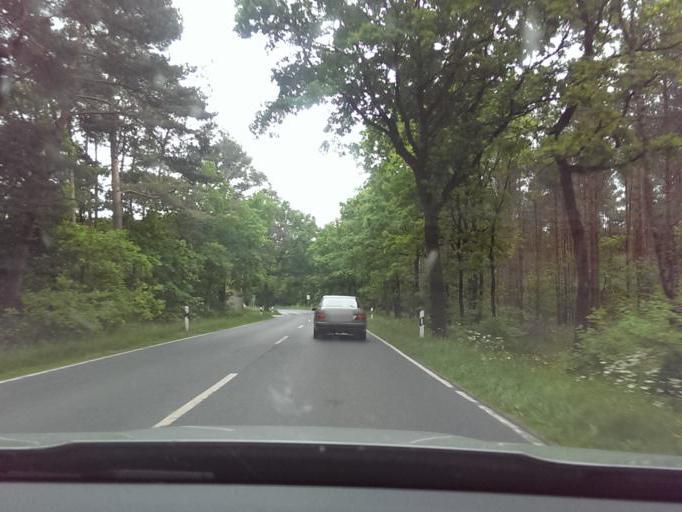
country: DE
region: Lower Saxony
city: Lindwedel
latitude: 52.6157
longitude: 9.7078
